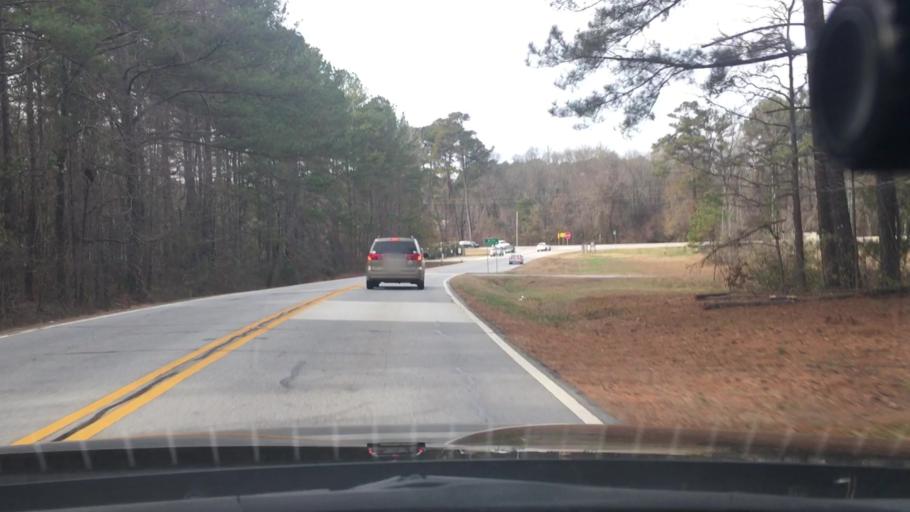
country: US
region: Georgia
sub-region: Coweta County
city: Senoia
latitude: 33.3279
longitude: -84.5049
